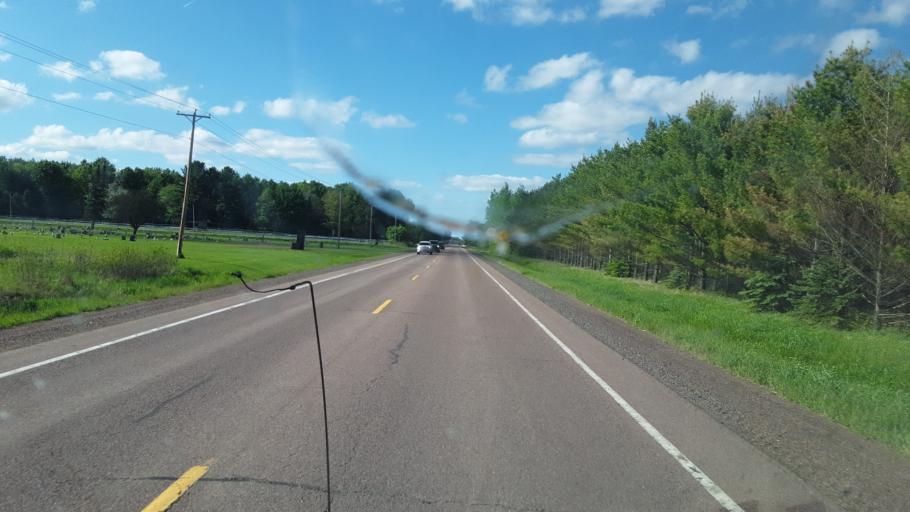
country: US
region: Wisconsin
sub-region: Wood County
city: Marshfield
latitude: 44.5678
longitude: -90.1806
